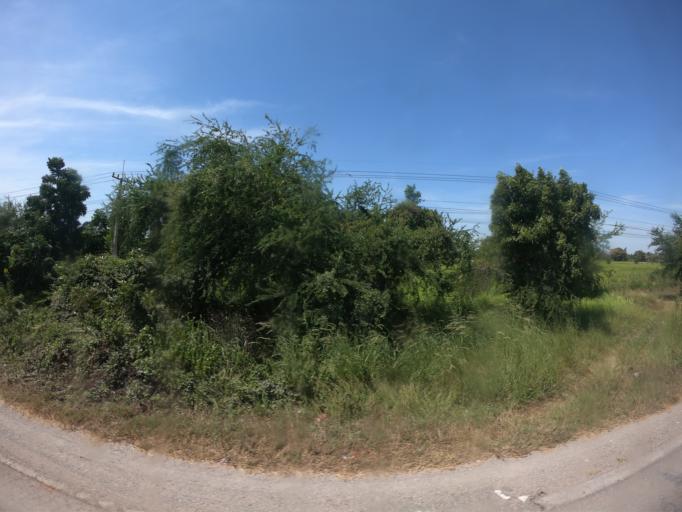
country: TH
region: Nakhon Ratchasima
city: Bua Lai
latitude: 15.6565
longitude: 102.5725
